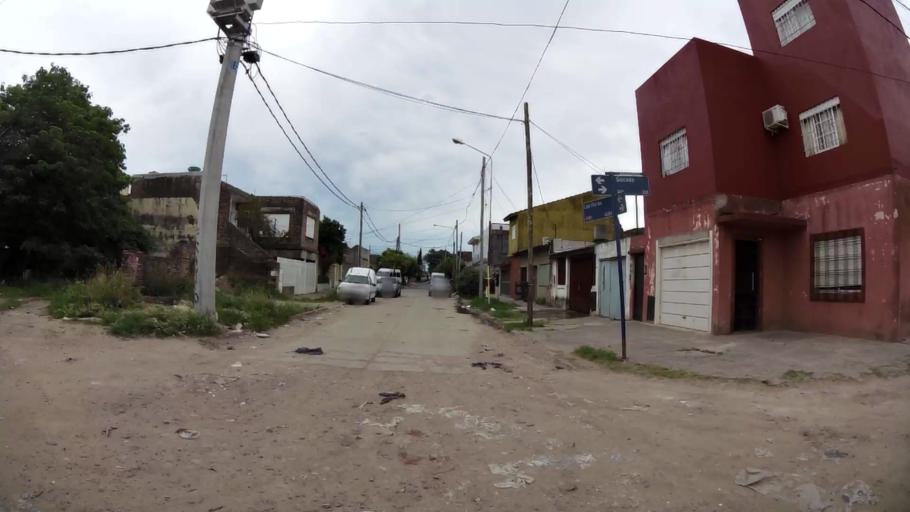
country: AR
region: Buenos Aires
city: San Justo
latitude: -34.6748
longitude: -58.5231
